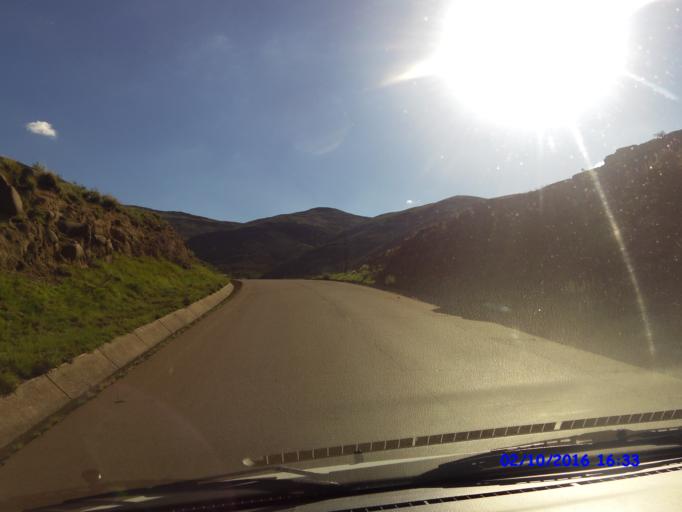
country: LS
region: Maseru
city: Nako
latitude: -29.4912
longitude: 28.0622
